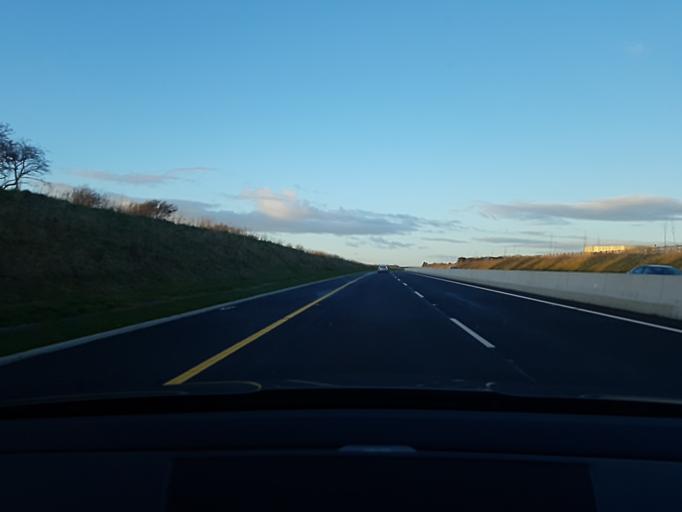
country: IE
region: Connaught
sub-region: County Galway
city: Athenry
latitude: 53.3286
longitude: -8.8033
